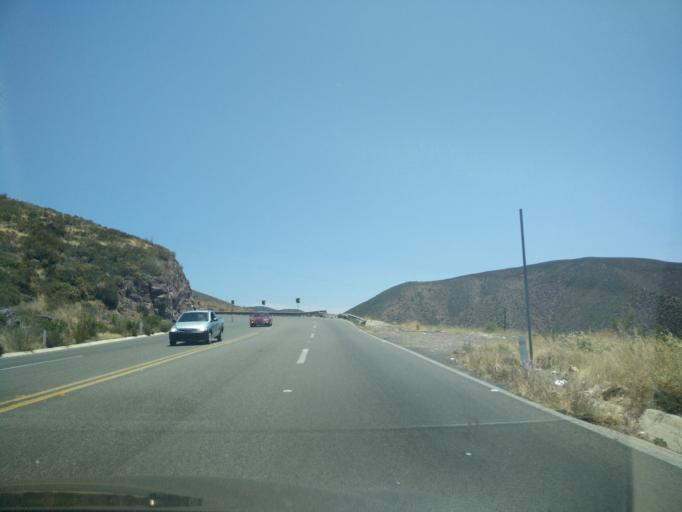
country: MX
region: Baja California
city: El Sauzal
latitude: 31.9283
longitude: -116.6702
